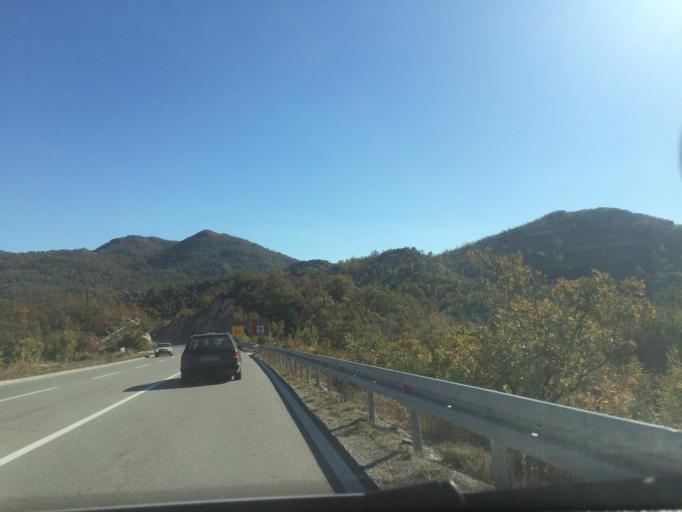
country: ME
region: Cetinje
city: Cetinje
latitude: 42.3781
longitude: 18.9868
